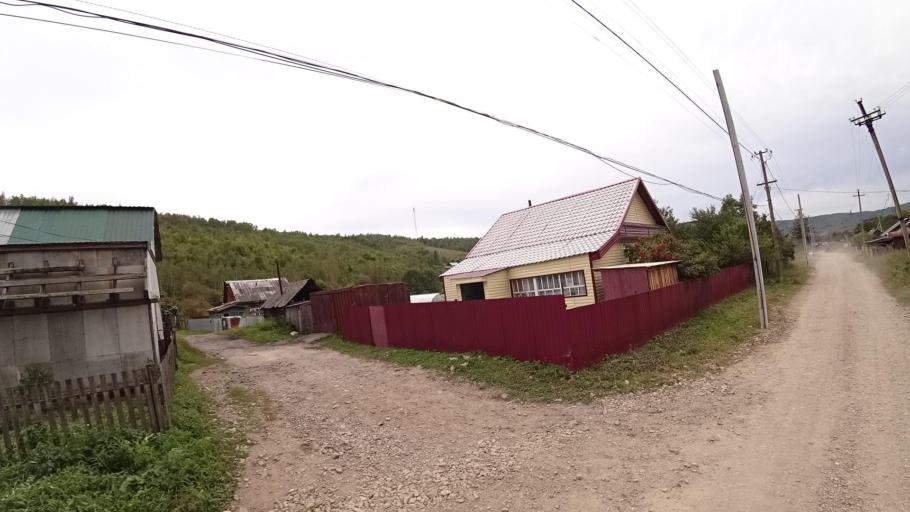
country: RU
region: Jewish Autonomous Oblast
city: Khingansk
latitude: 49.0234
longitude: 131.0699
